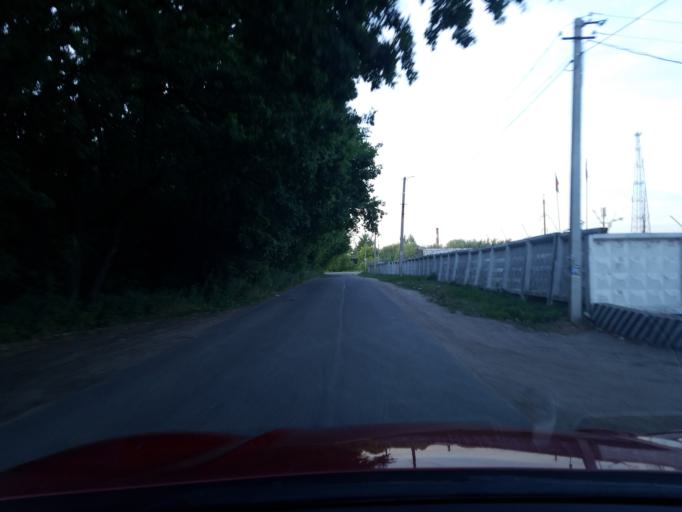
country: RU
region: Orjol
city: Znamenka
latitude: 52.9134
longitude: 36.0071
